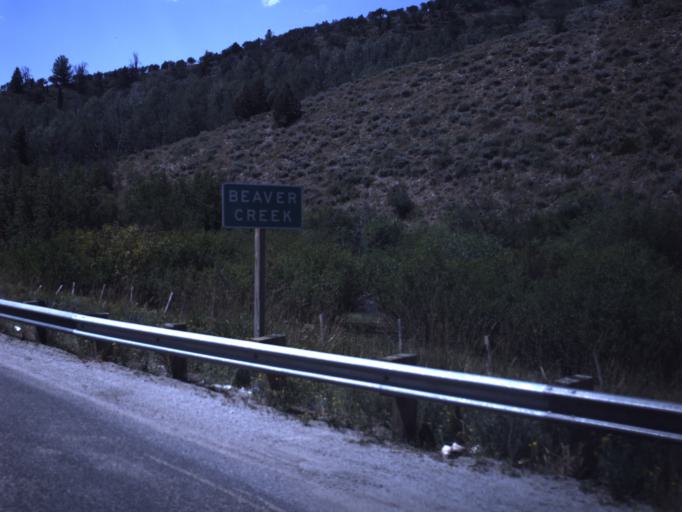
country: US
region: Utah
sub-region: Cache County
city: Richmond
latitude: 41.9385
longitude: -111.5549
